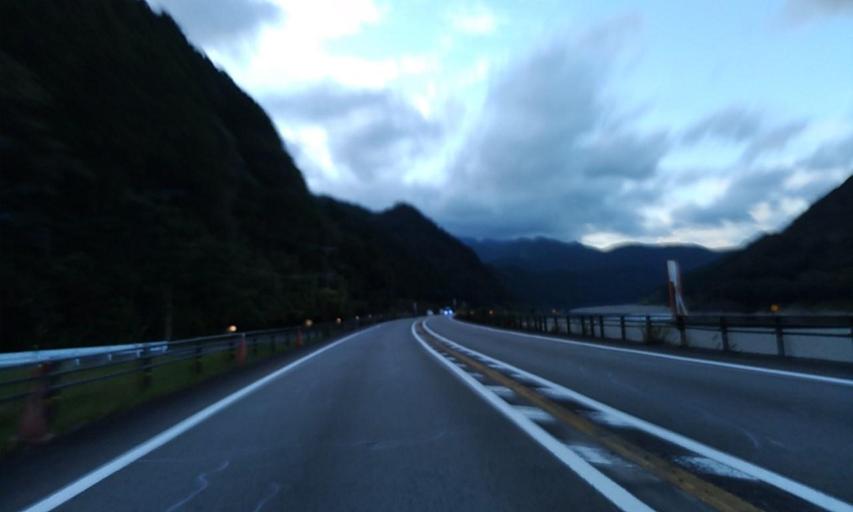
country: JP
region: Wakayama
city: Shingu
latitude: 33.7258
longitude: 135.9559
